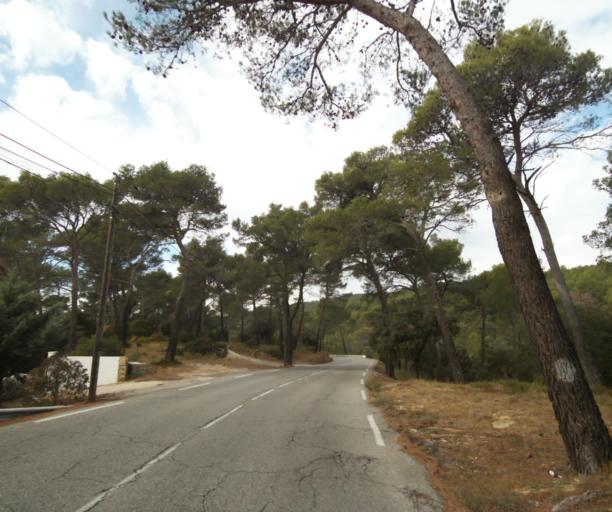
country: FR
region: Provence-Alpes-Cote d'Azur
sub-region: Departement des Bouches-du-Rhone
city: Ceyreste
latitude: 43.2317
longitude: 5.6598
